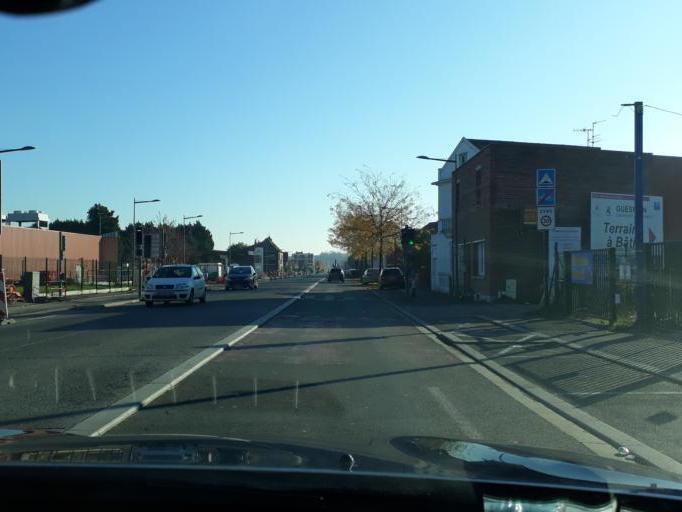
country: FR
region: Nord-Pas-de-Calais
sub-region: Departement du Nord
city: Guesnain
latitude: 50.3468
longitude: 3.1467
